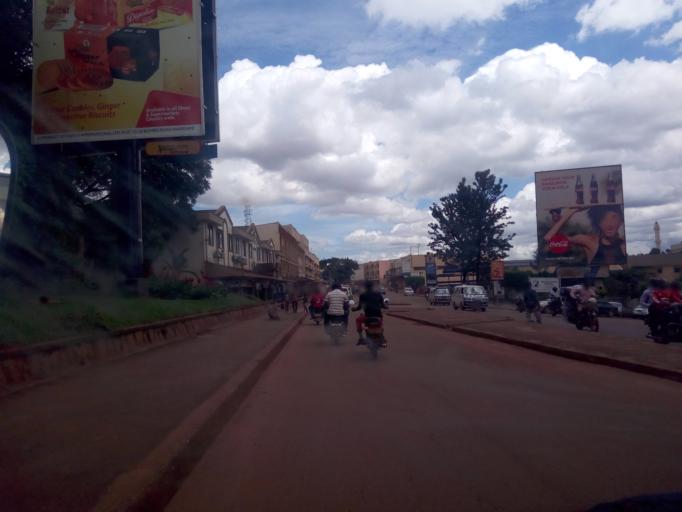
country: UG
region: Central Region
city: Kampala Central Division
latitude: 0.3209
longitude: 32.5740
